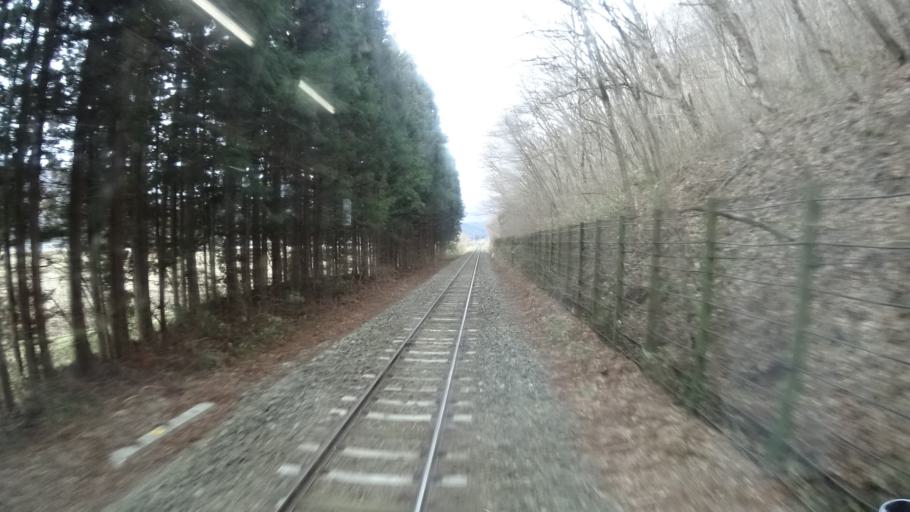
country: JP
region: Iwate
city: Tono
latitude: 39.3081
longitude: 141.4199
